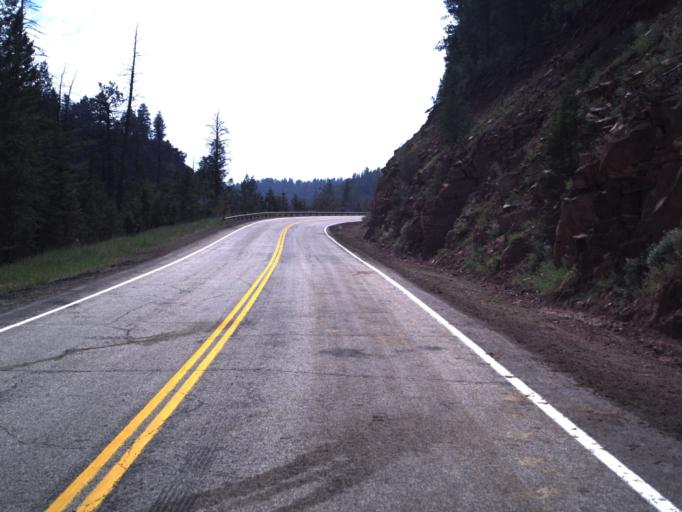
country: US
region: Utah
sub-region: Daggett County
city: Manila
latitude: 40.8711
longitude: -109.6912
